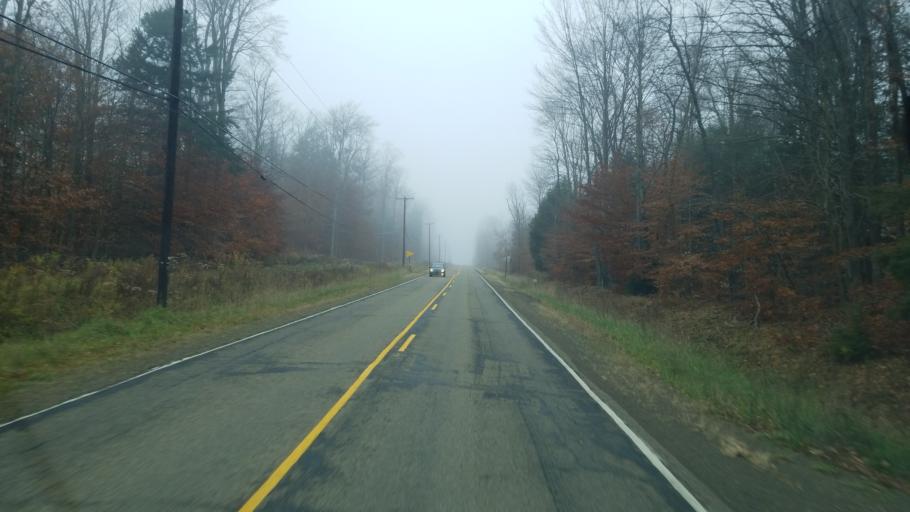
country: US
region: Pennsylvania
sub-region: McKean County
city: Smethport
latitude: 41.8144
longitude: -78.5510
